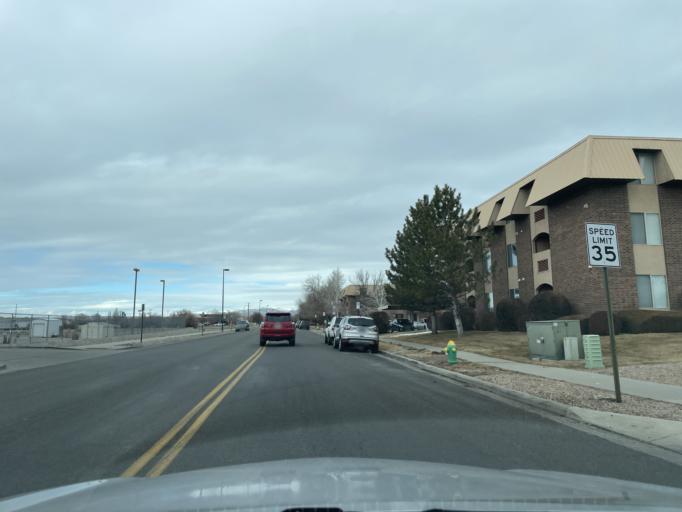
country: US
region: Colorado
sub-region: Mesa County
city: Grand Junction
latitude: 39.0925
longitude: -108.5802
